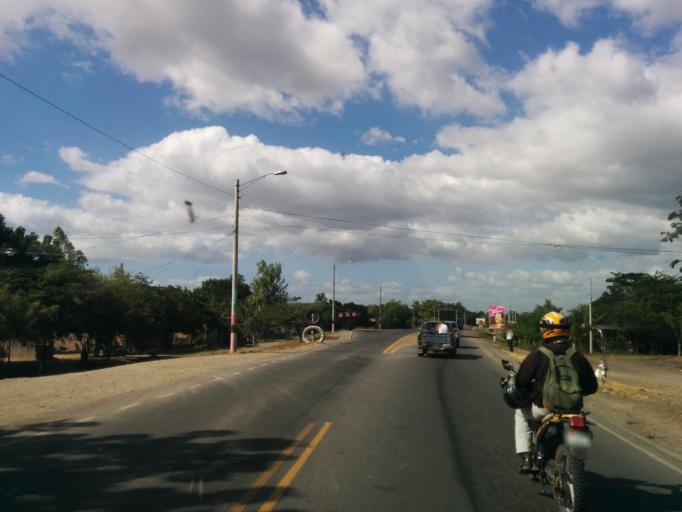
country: NI
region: Matagalpa
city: Ciudad Dario
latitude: 12.6659
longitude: -86.0873
